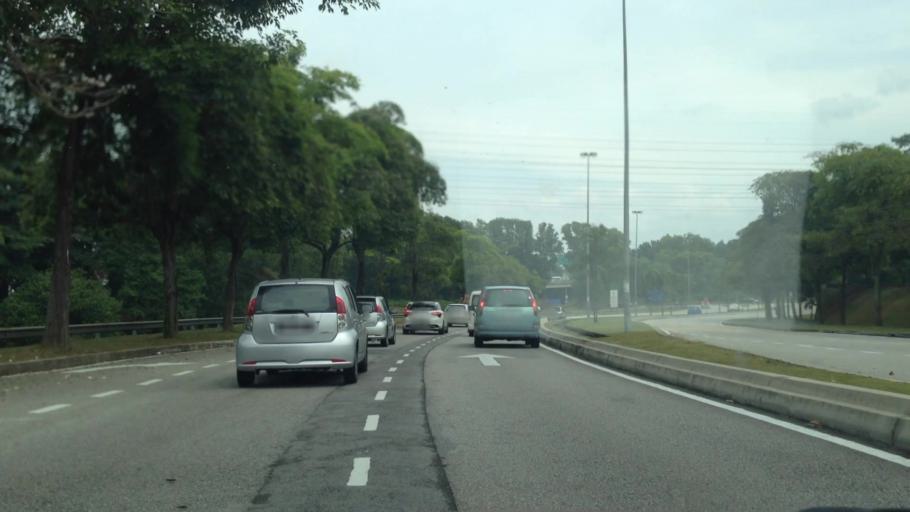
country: MY
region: Selangor
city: Subang Jaya
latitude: 3.0449
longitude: 101.5714
